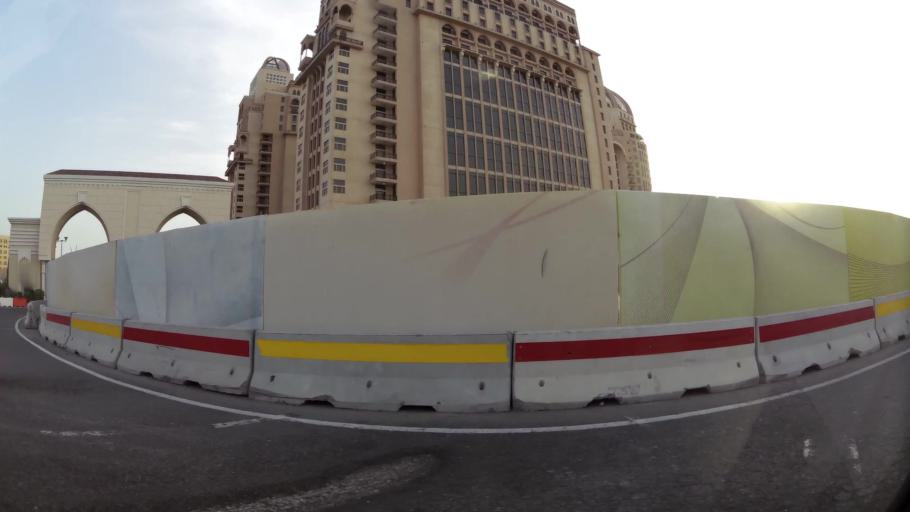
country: QA
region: Baladiyat ad Dawhah
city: Doha
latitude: 25.3514
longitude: 51.5286
